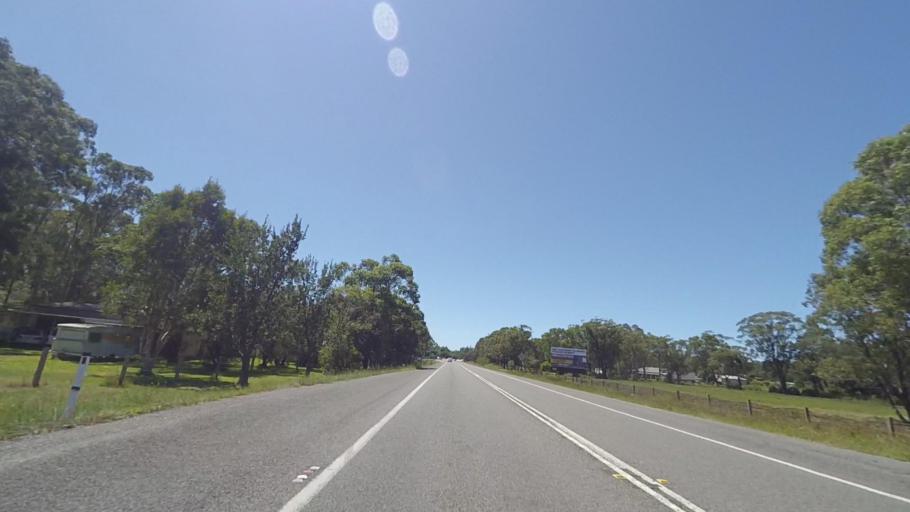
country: AU
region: New South Wales
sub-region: Port Stephens Shire
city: Medowie
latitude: -32.7870
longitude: 151.8995
